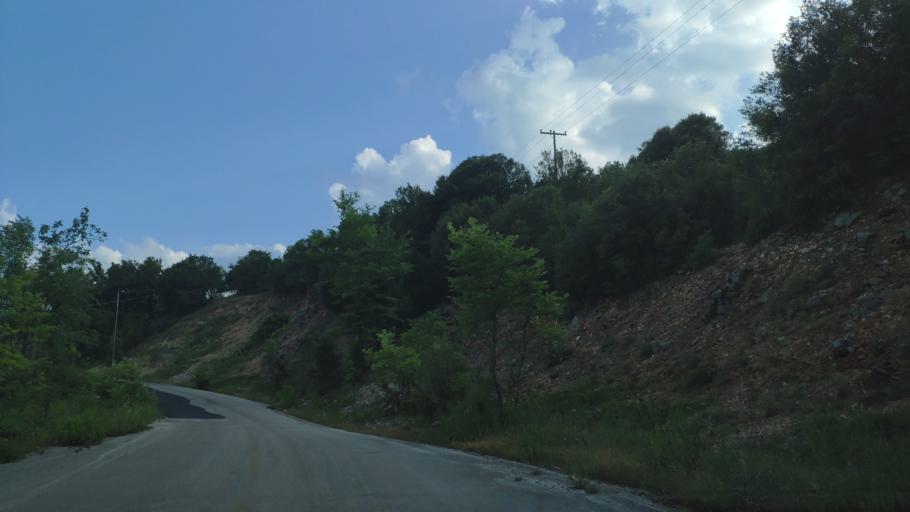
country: GR
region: Epirus
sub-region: Nomos Artas
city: Agios Dimitrios
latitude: 39.3743
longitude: 21.0249
